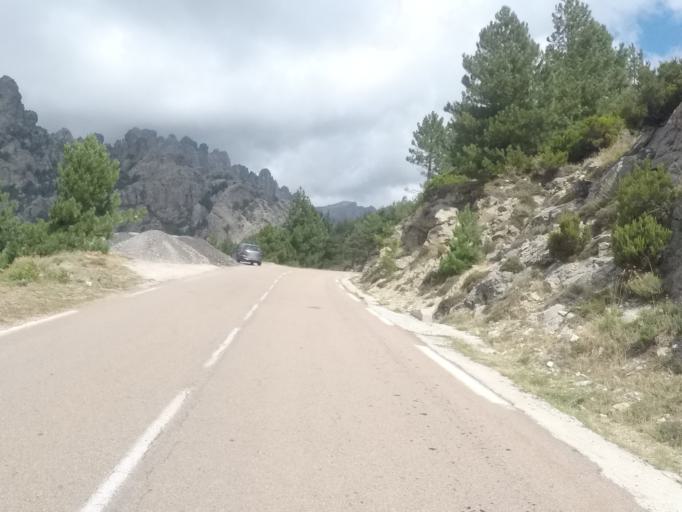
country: FR
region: Corsica
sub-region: Departement de la Corse-du-Sud
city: Zonza
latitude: 41.7895
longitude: 9.2218
